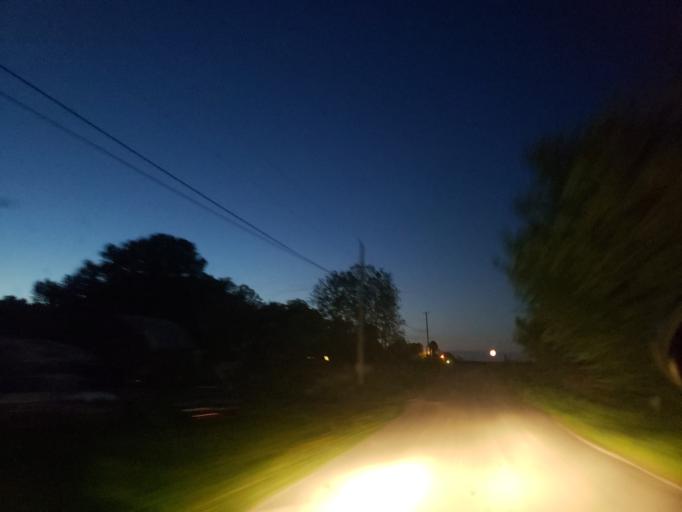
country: US
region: Alabama
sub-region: Madison County
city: Hazel Green
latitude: 34.9760
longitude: -86.6681
